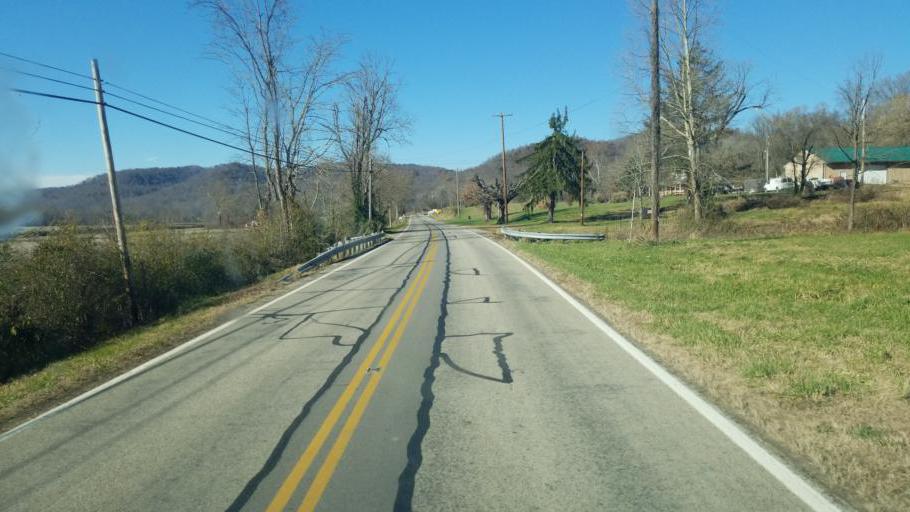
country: US
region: Kentucky
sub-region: Lewis County
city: Vanceburg
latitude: 38.6341
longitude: -83.2152
